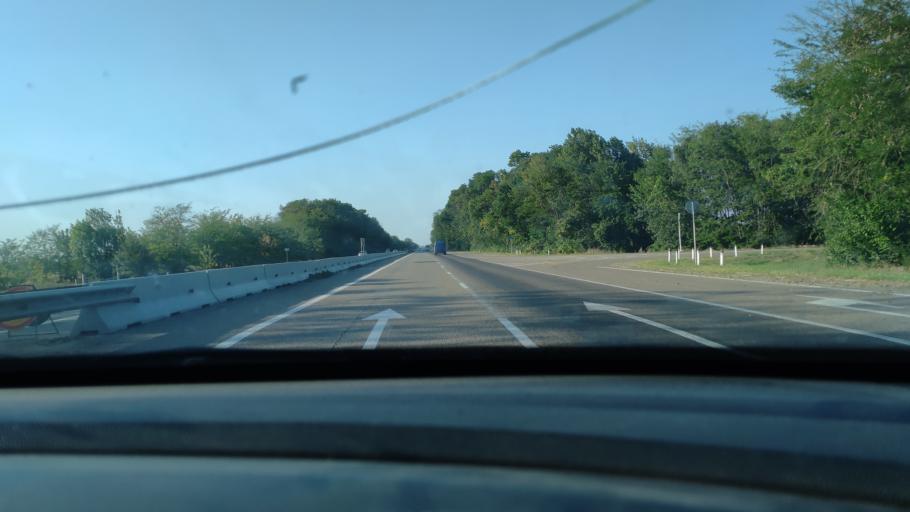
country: RU
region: Krasnodarskiy
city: Timashevsk
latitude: 45.5370
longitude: 38.9372
